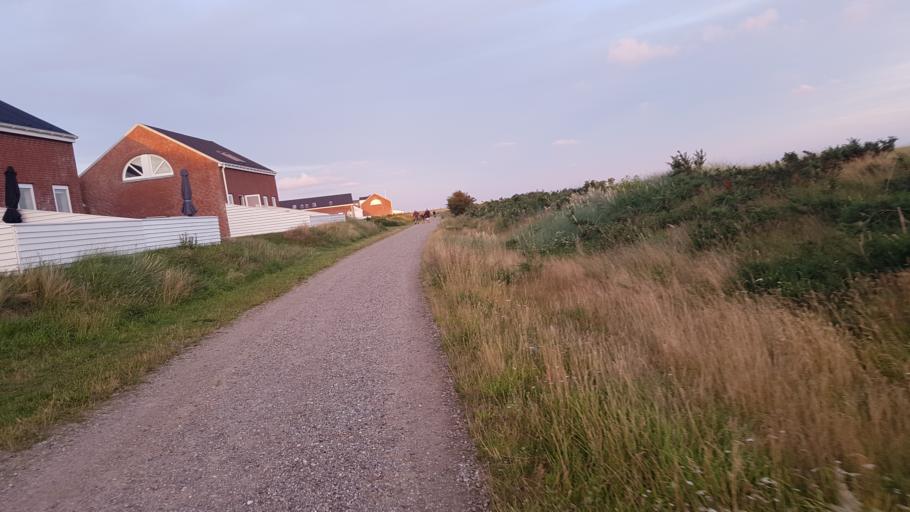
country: DE
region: Schleswig-Holstein
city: List
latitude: 55.0861
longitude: 8.5473
